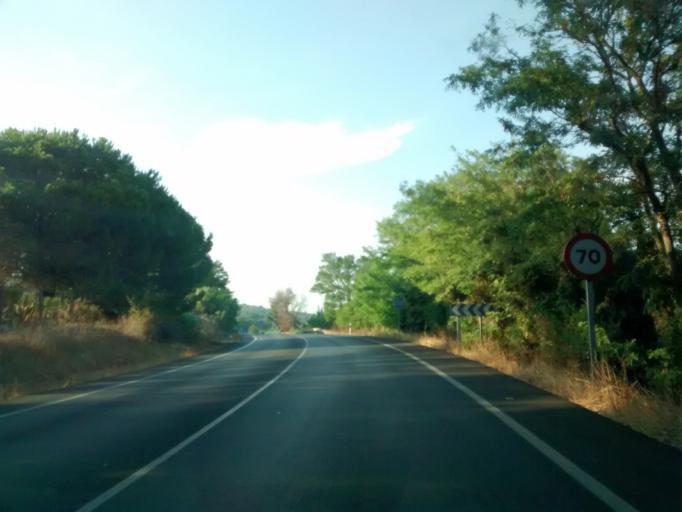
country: ES
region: Andalusia
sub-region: Provincia de Cadiz
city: Vejer de la Frontera
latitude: 36.2305
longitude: -5.9487
